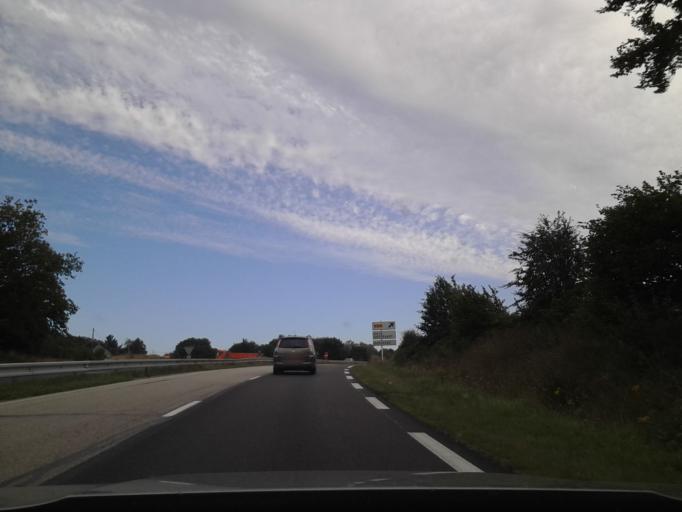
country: FR
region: Lower Normandy
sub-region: Departement de la Manche
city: Brix
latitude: 49.5531
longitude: -1.5615
